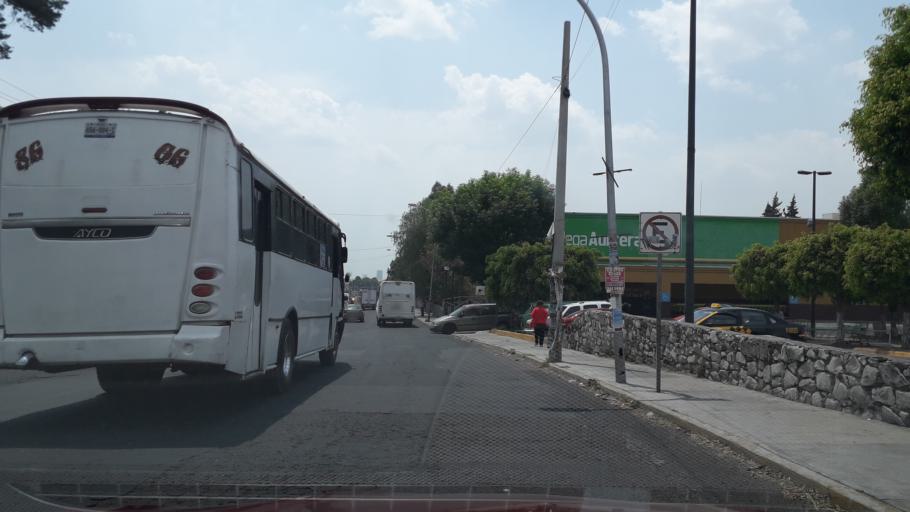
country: MX
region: Puebla
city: Puebla
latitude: 19.0458
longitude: -98.1799
